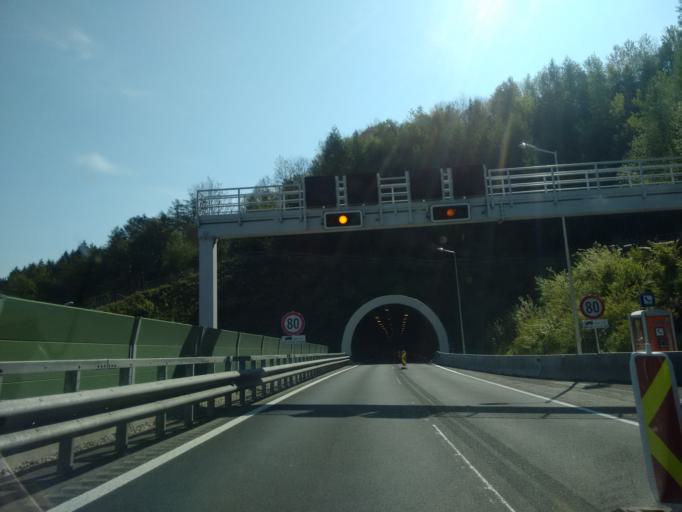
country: AT
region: Styria
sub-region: Politischer Bezirk Bruck-Muerzzuschlag
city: Bruck an der Mur
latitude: 47.4025
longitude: 15.2567
